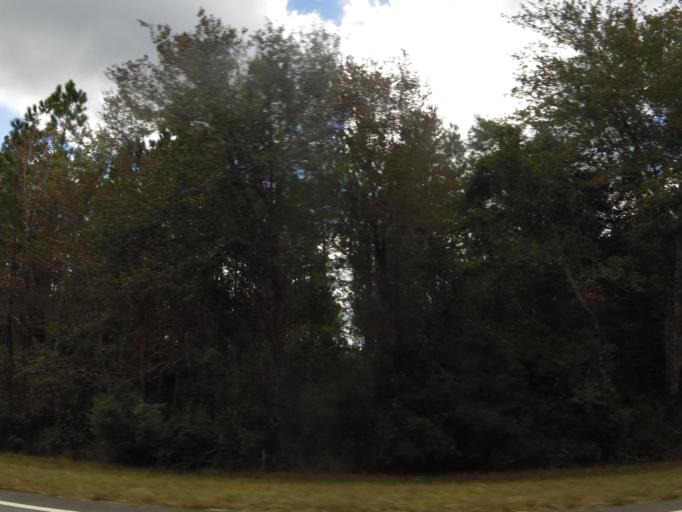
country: US
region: Georgia
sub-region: Charlton County
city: Folkston
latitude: 30.9022
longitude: -82.0175
